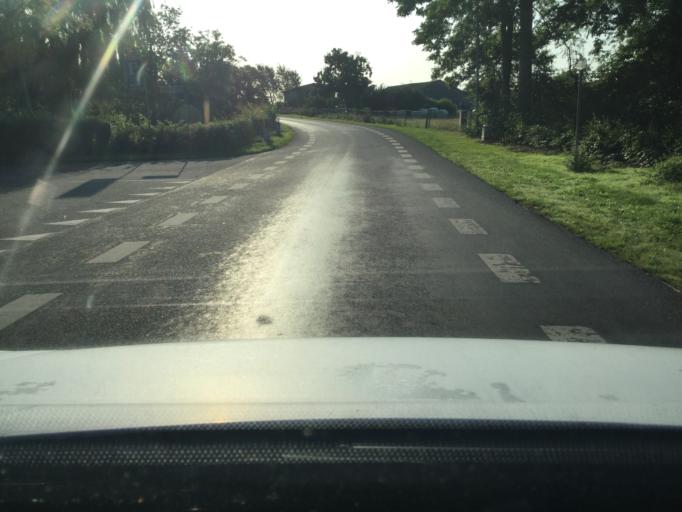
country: DK
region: Zealand
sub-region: Lolland Kommune
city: Rodby
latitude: 54.7089
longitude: 11.3859
